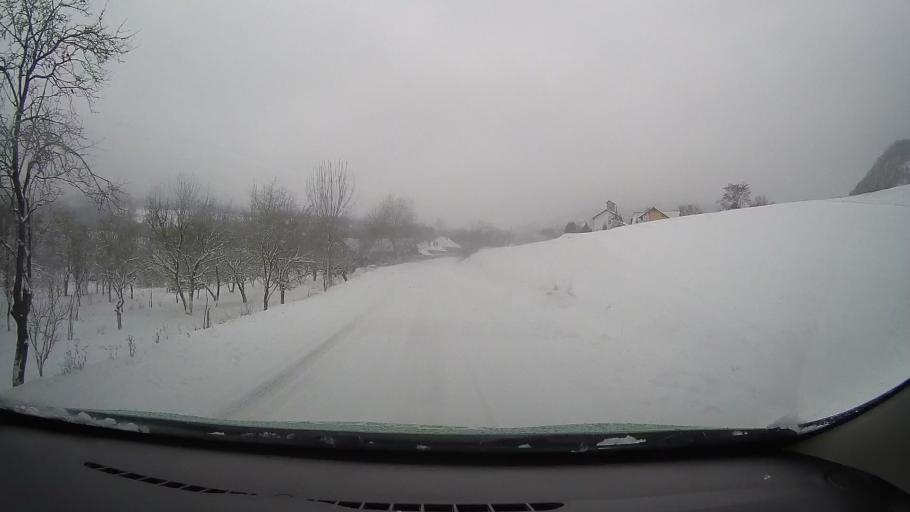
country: RO
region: Hunedoara
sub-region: Comuna Carjiti
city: Carjiti
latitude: 45.8434
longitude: 22.8317
